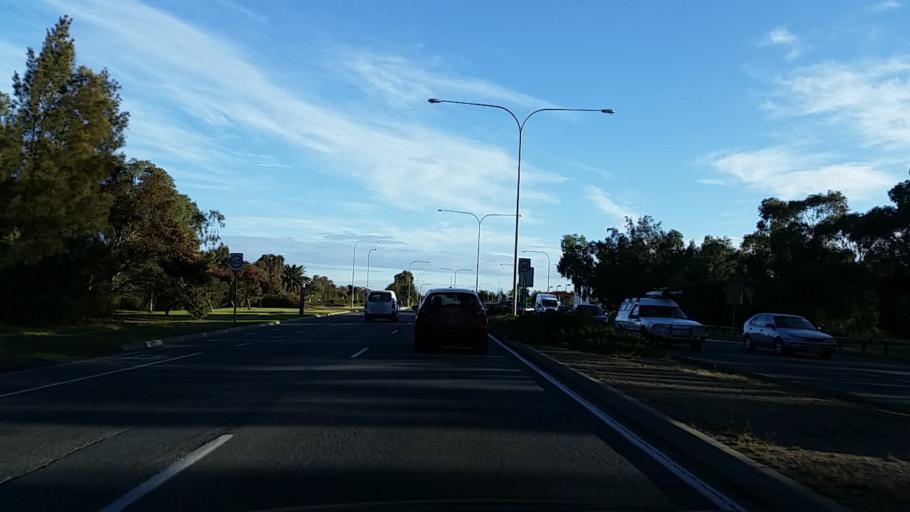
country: AU
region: South Australia
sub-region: Salisbury
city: Salisbury
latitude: -34.7965
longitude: 138.6109
